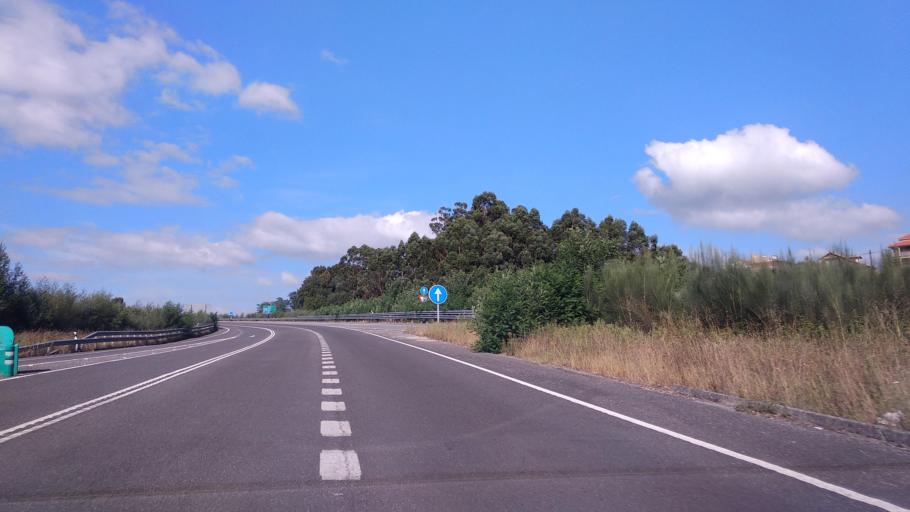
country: ES
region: Galicia
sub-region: Provincia de Pontevedra
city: Moana
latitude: 42.2772
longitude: -8.7541
